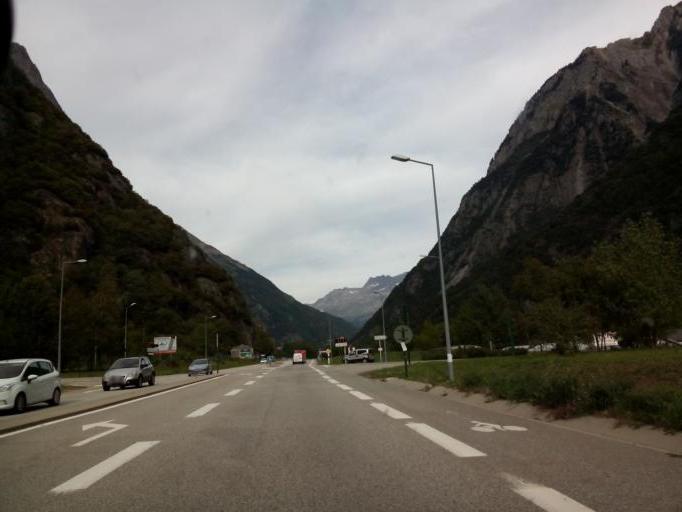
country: FR
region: Rhone-Alpes
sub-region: Departement de l'Isere
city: Livet-et-Gavet
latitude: 45.1086
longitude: 5.9389
